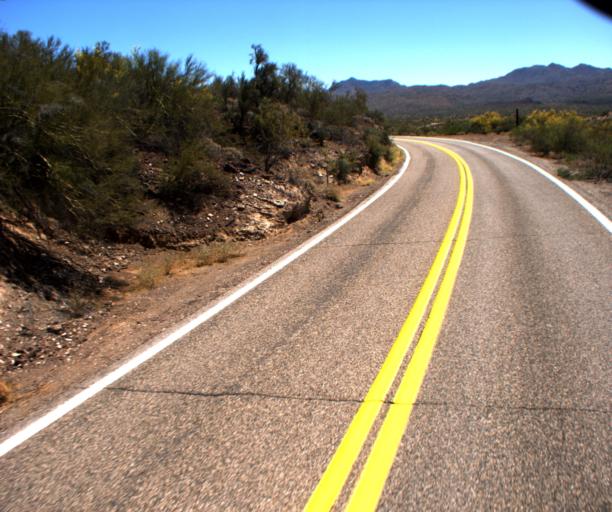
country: US
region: Arizona
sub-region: Yavapai County
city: Bagdad
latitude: 34.4985
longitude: -113.0688
